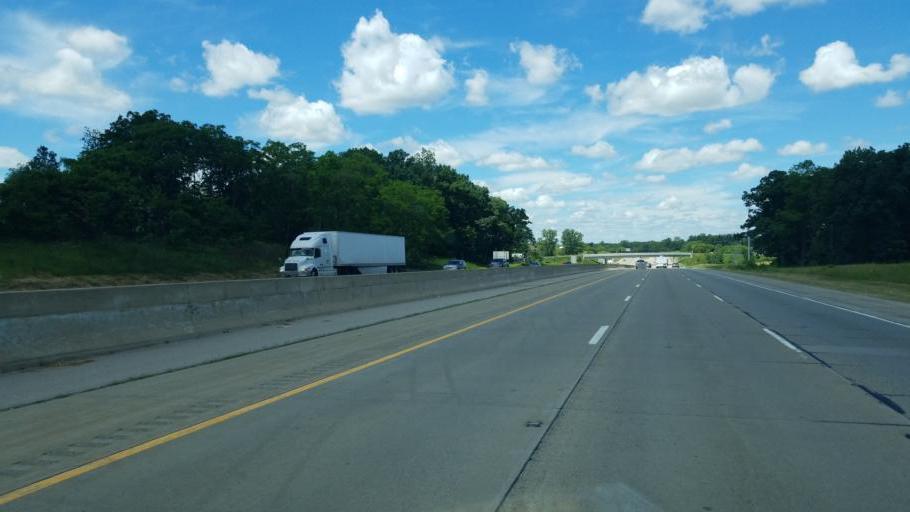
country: US
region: Michigan
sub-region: Livingston County
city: Howell
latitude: 42.5796
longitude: -83.8917
